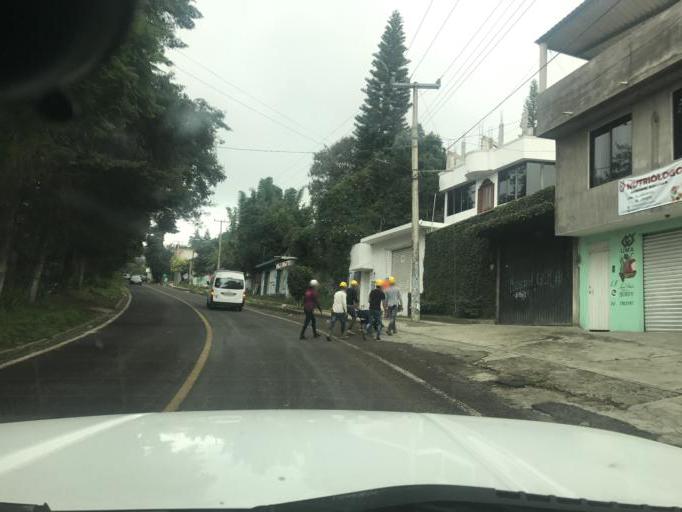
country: MX
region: Morelos
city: Ocuituco
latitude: 18.8800
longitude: -98.7718
